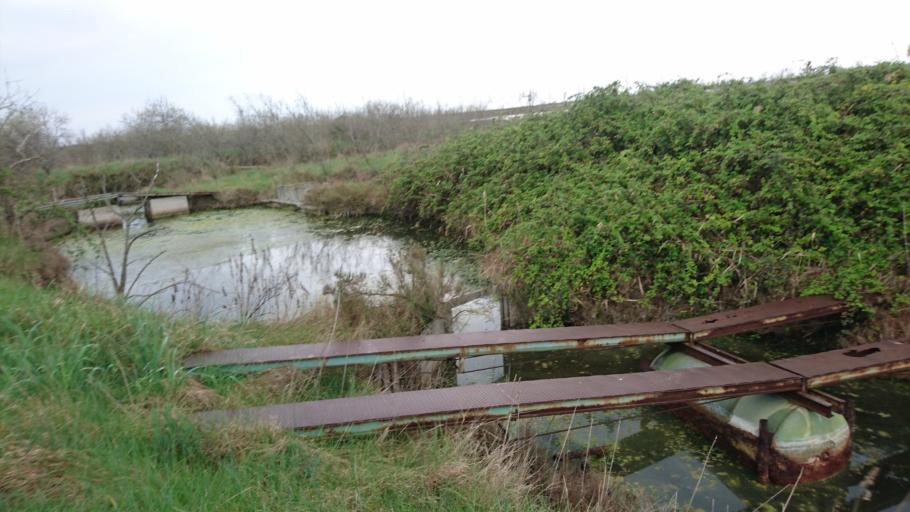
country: IT
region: Veneto
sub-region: Provincia di Venezia
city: Ca' Savio
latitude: 45.4917
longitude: 12.4890
